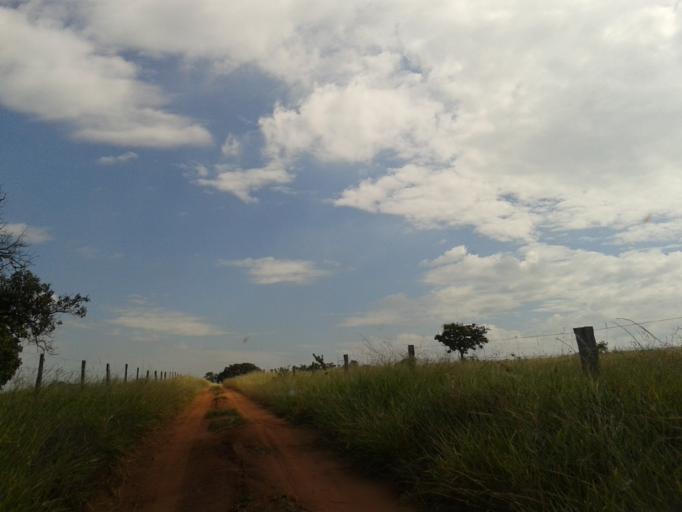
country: BR
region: Minas Gerais
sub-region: Campina Verde
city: Campina Verde
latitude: -19.3925
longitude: -49.6416
